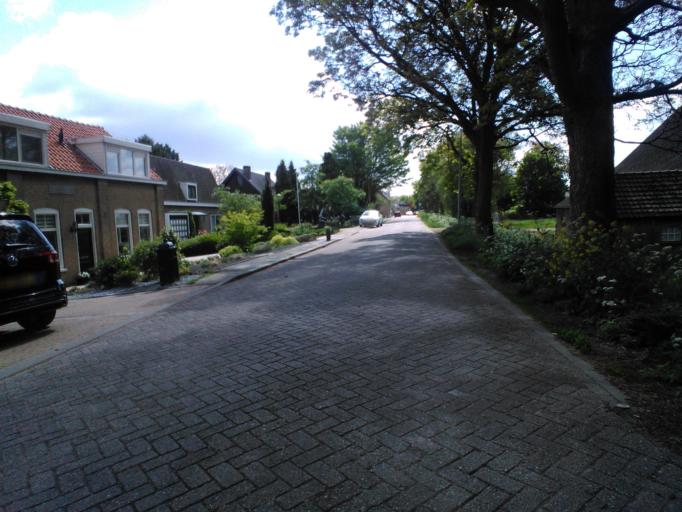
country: NL
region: South Holland
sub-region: Gemeente Hendrik-Ido-Ambacht
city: Hendrik-Ido-Ambacht
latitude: 51.8530
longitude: 4.6387
